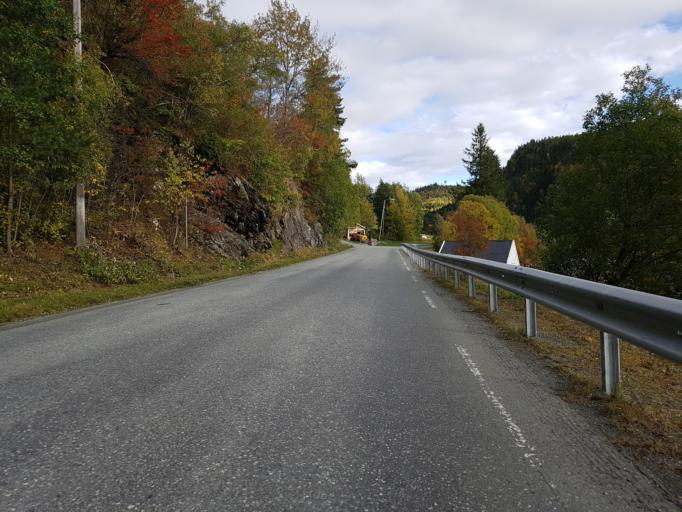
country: NO
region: Sor-Trondelag
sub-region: Klaebu
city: Klaebu
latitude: 63.3977
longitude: 10.5495
